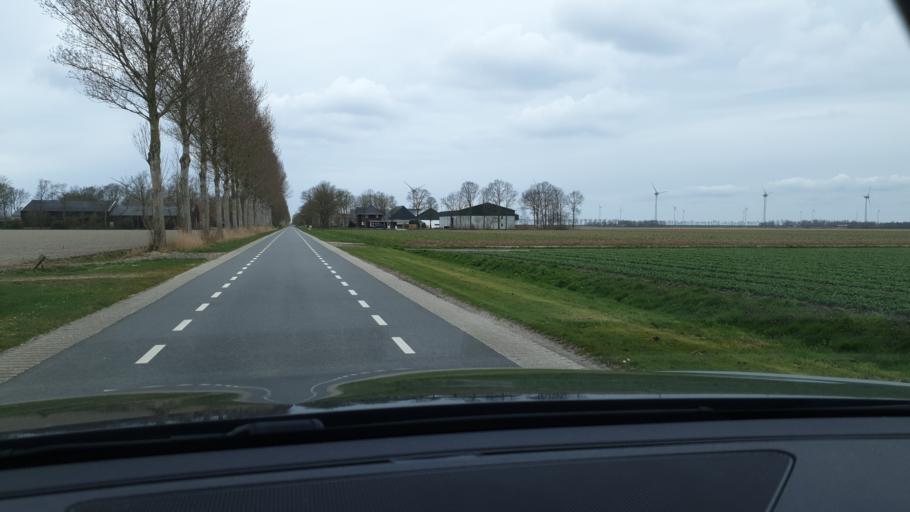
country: NL
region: Flevoland
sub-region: Gemeente Urk
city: Urk
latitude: 52.7252
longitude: 5.6367
